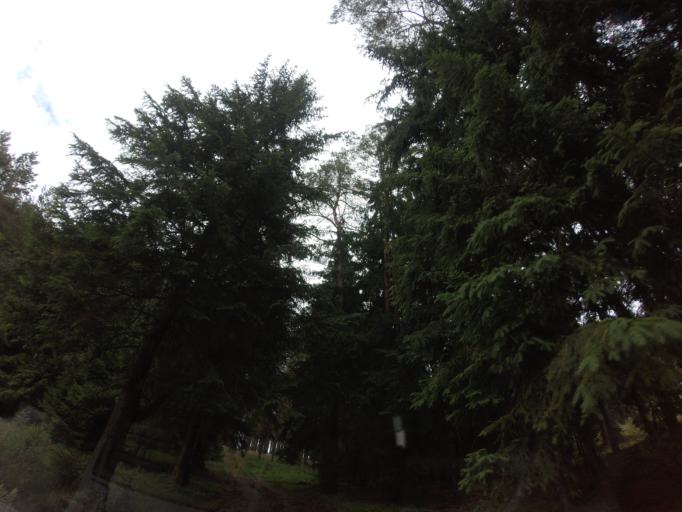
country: PL
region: West Pomeranian Voivodeship
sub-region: Powiat choszczenski
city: Drawno
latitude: 53.1466
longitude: 15.7688
